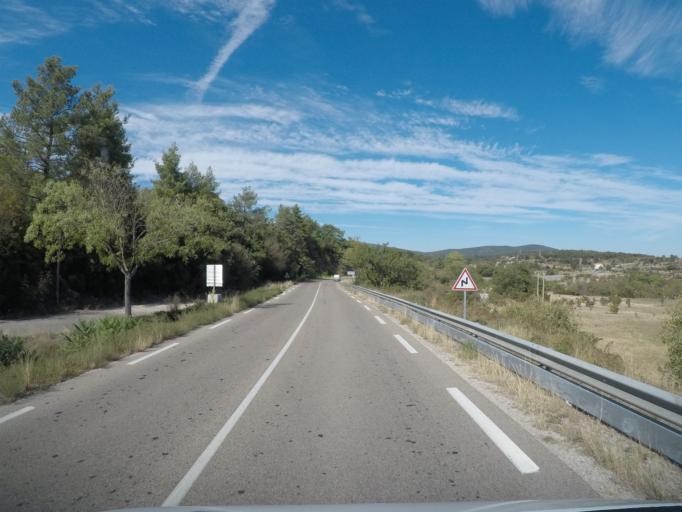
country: FR
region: Languedoc-Roussillon
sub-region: Departement de l'Herault
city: Saint-Martin-de-Londres
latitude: 43.8095
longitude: 3.7416
